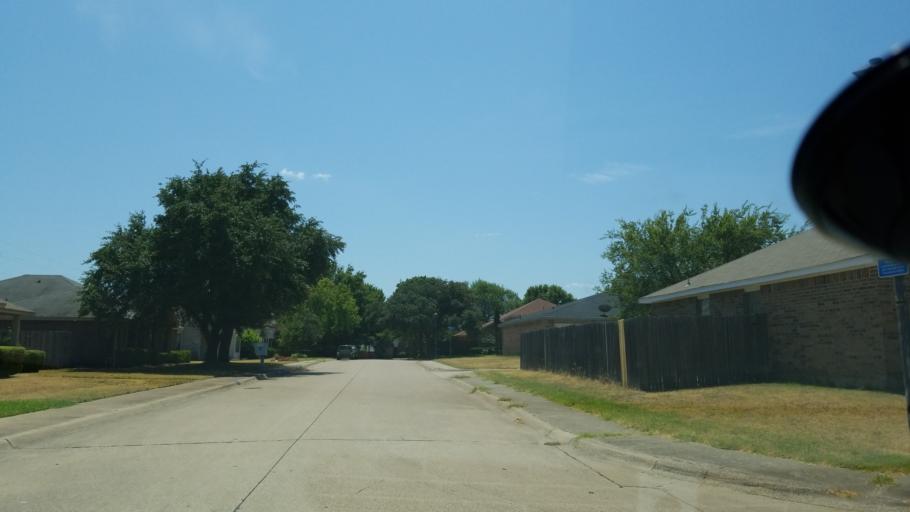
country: US
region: Texas
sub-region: Dallas County
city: Duncanville
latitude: 32.6388
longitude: -96.8866
